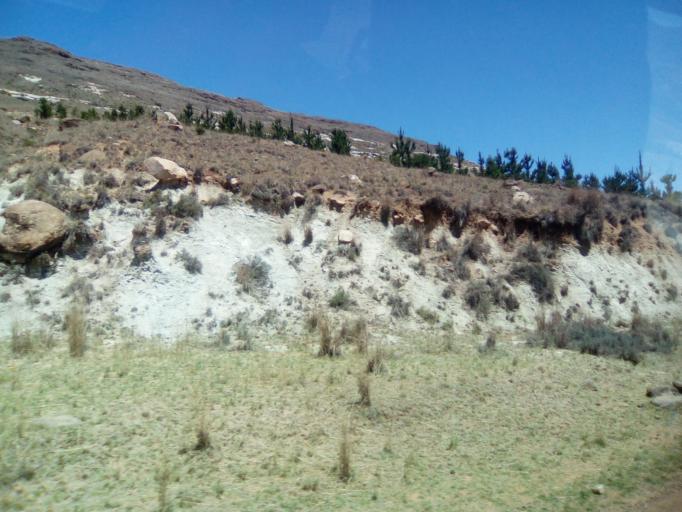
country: LS
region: Qacha's Nek
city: Qacha's Nek
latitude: -30.0379
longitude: 28.6752
